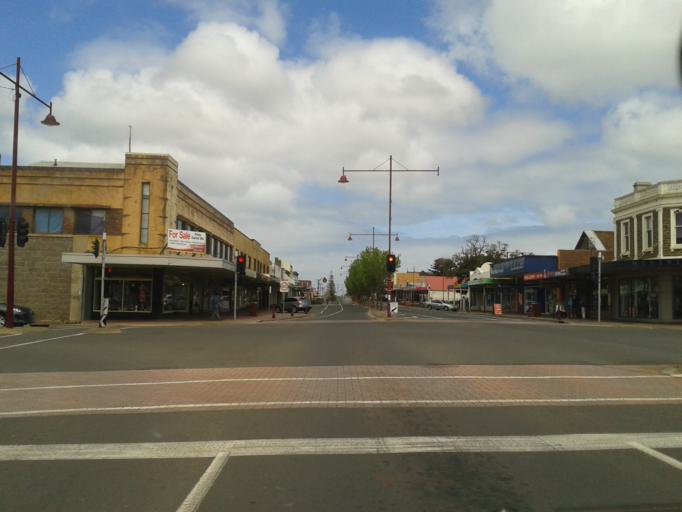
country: AU
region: Victoria
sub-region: Glenelg
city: Portland
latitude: -38.3461
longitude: 141.6038
